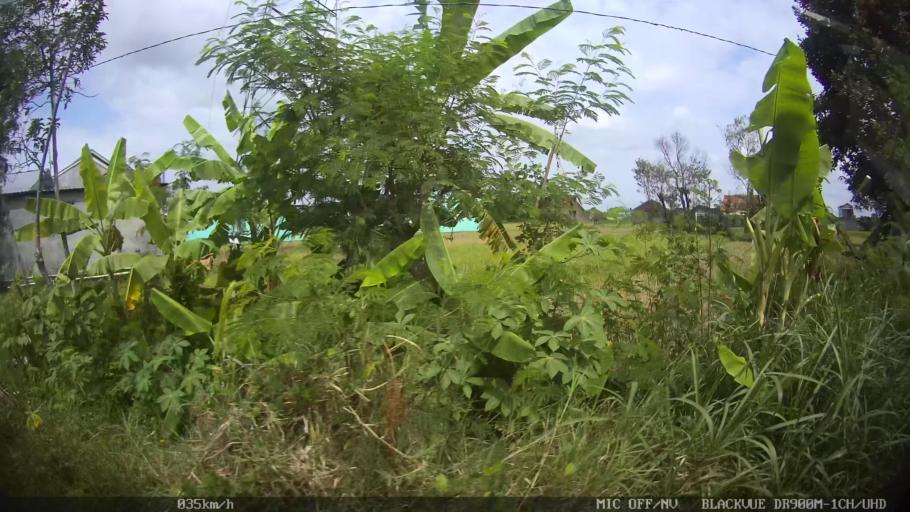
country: ID
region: Central Java
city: Candi Prambanan
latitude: -7.7853
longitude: 110.4795
